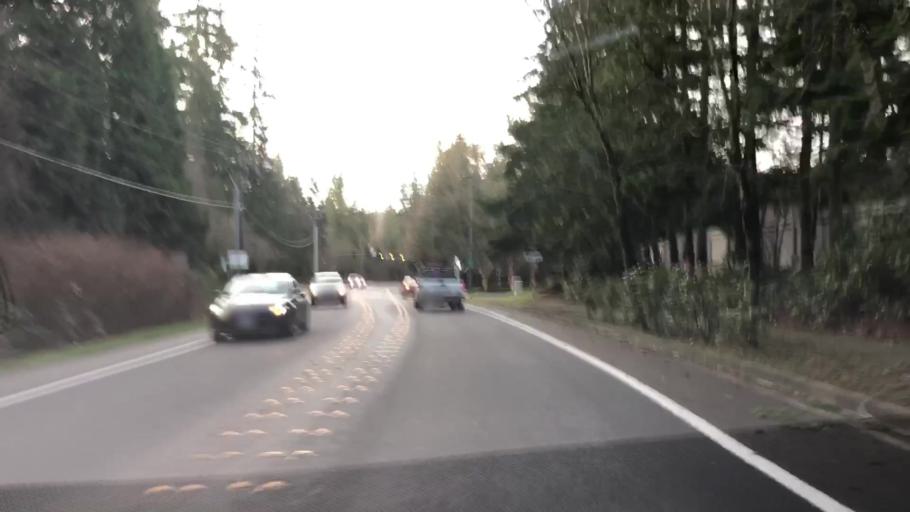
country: US
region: Washington
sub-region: King County
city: Newcastle
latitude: 47.5482
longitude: -122.1292
